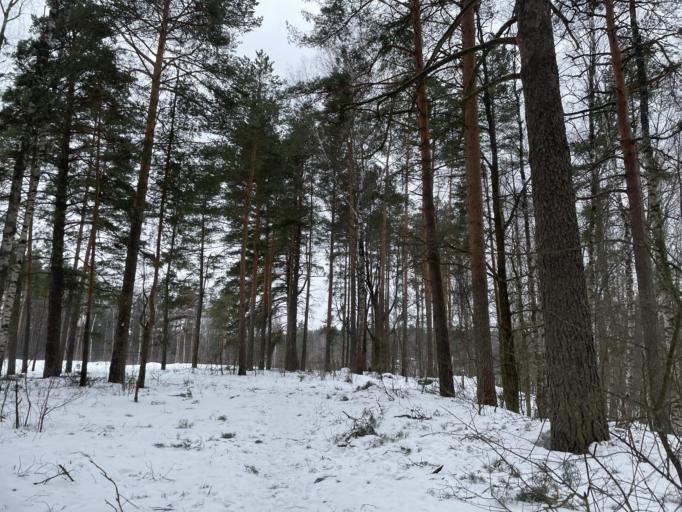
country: RU
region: Vladimir
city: Pokrov
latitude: 55.9416
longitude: 39.2376
